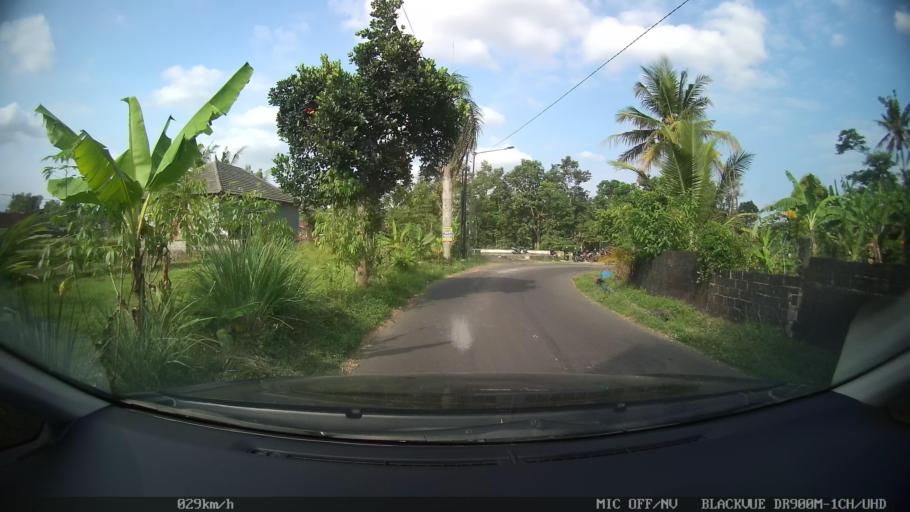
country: ID
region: Daerah Istimewa Yogyakarta
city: Depok
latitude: -7.7222
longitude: 110.4391
